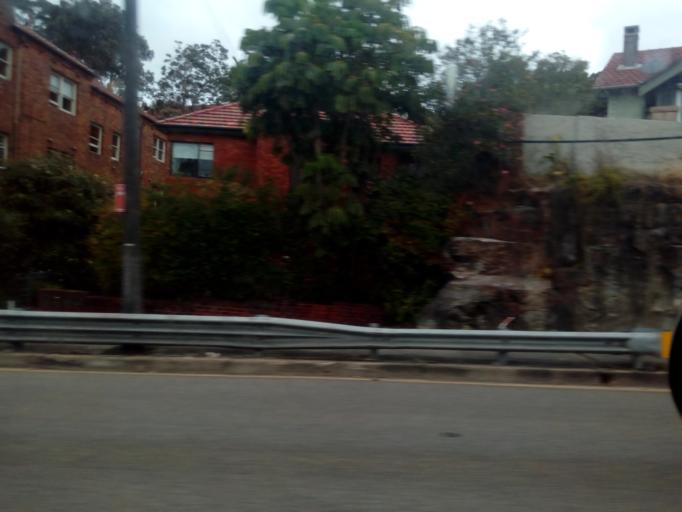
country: AU
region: New South Wales
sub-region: North Sydney
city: Cammeray
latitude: -33.8186
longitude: 151.2119
